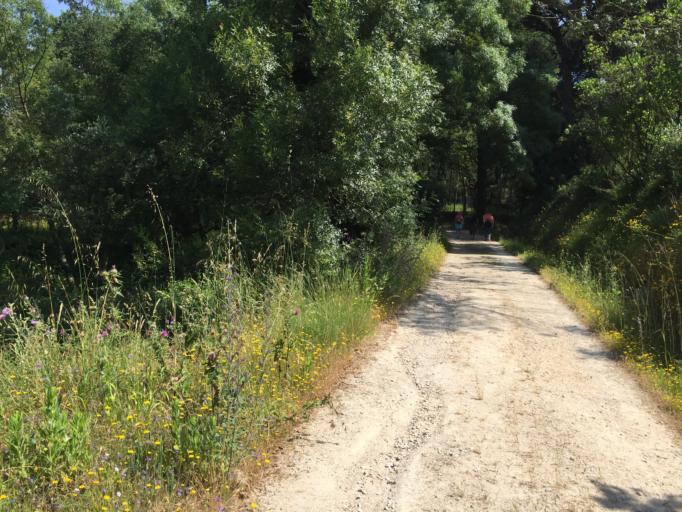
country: PT
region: Lisbon
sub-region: Mafra
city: Milharado
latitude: 38.9061
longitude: -9.1869
